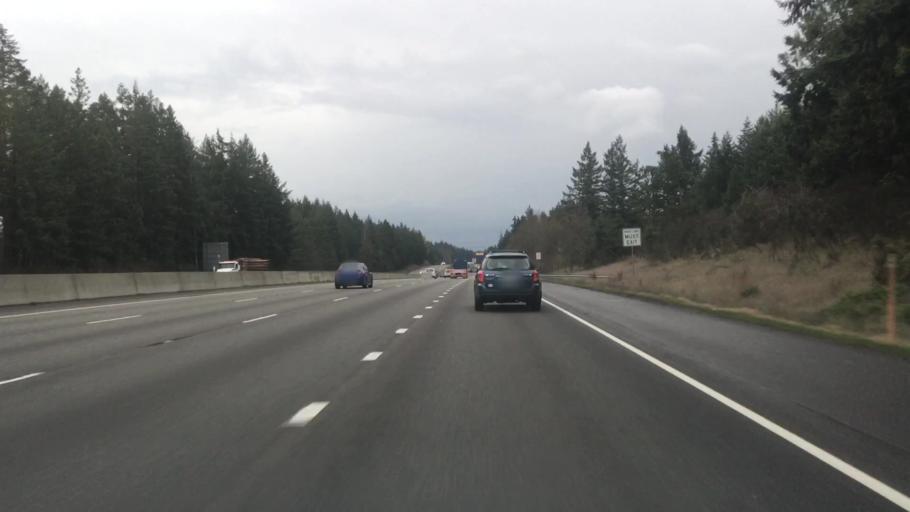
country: US
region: Washington
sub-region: Thurston County
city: Grand Mound
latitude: 46.8792
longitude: -122.9667
